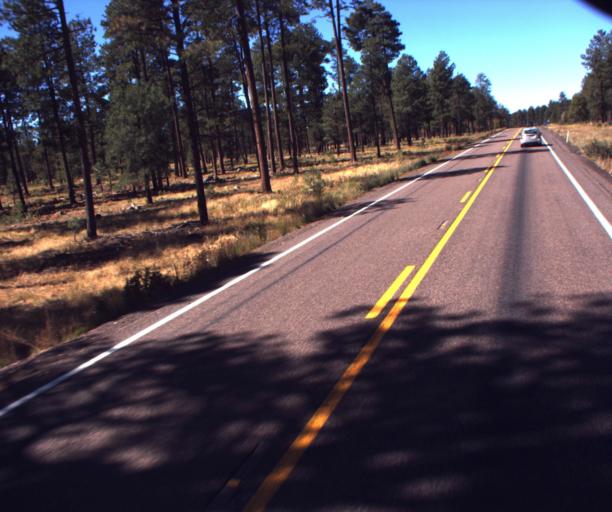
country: US
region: Arizona
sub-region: Navajo County
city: Heber-Overgaard
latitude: 34.3008
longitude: -110.8789
